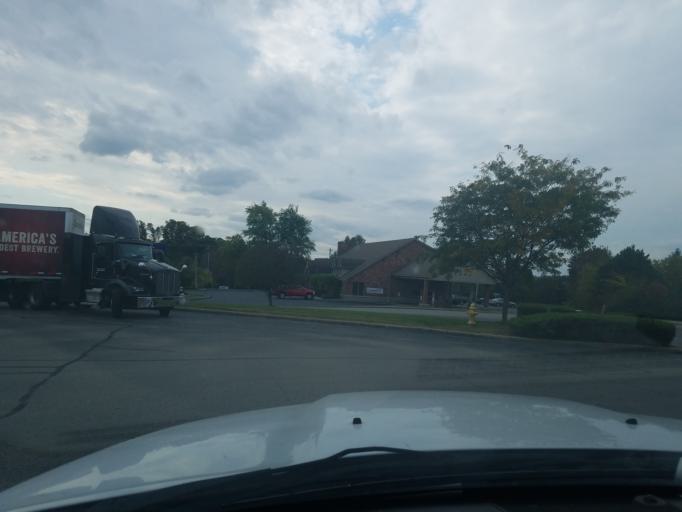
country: US
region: Indiana
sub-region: Clark County
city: Clarksville
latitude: 38.3409
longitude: -85.8003
